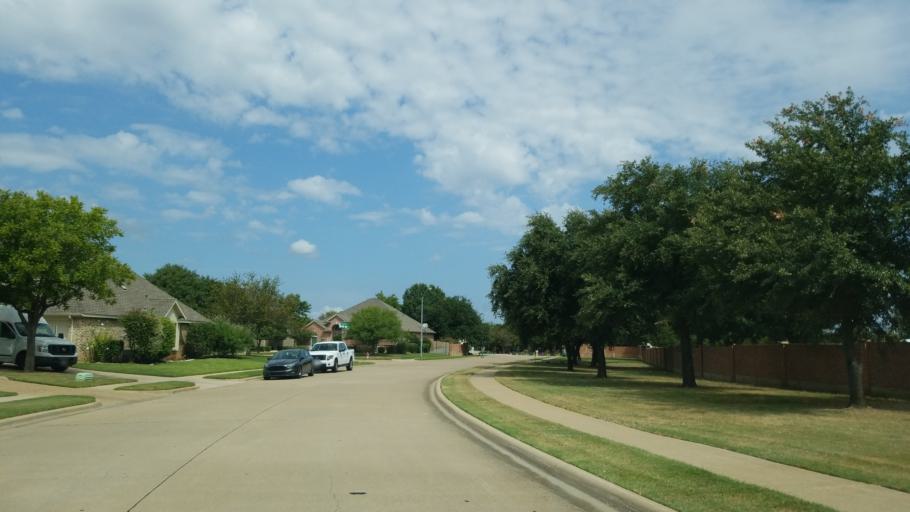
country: US
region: Texas
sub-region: Tarrant County
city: Grapevine
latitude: 32.8989
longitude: -97.1015
